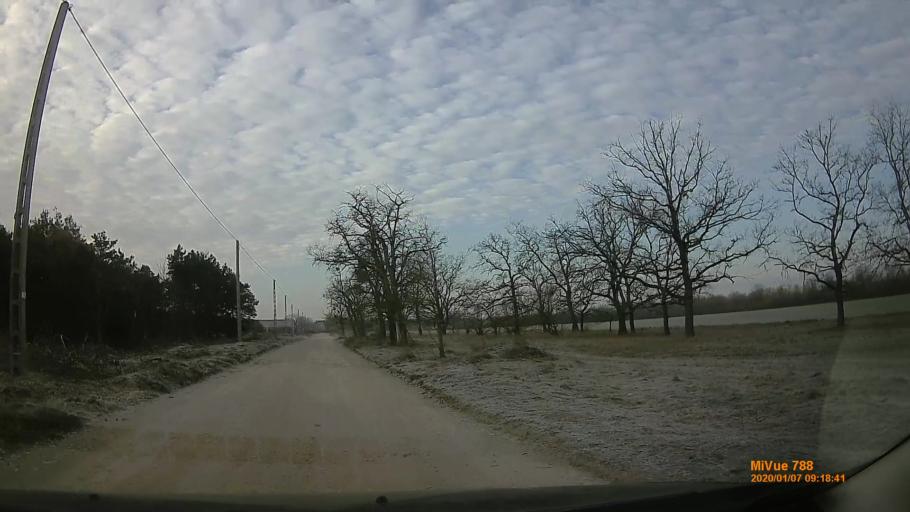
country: HU
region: Gyor-Moson-Sopron
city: Rajka
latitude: 47.9596
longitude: 17.1662
